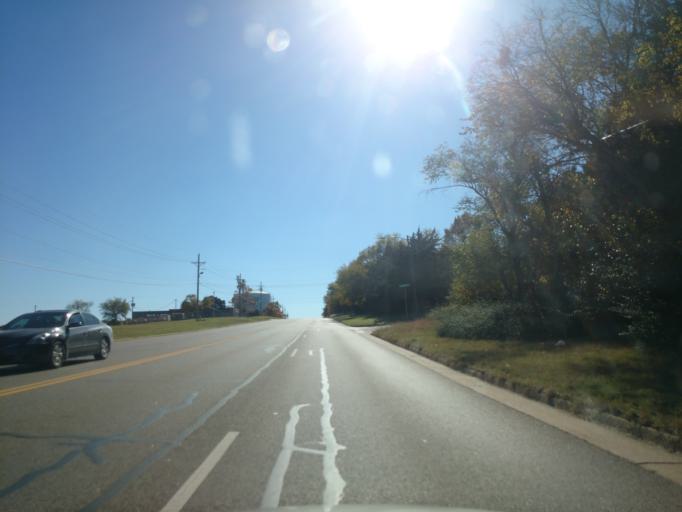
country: US
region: Oklahoma
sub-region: Payne County
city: Stillwater
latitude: 36.1519
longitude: -97.0697
